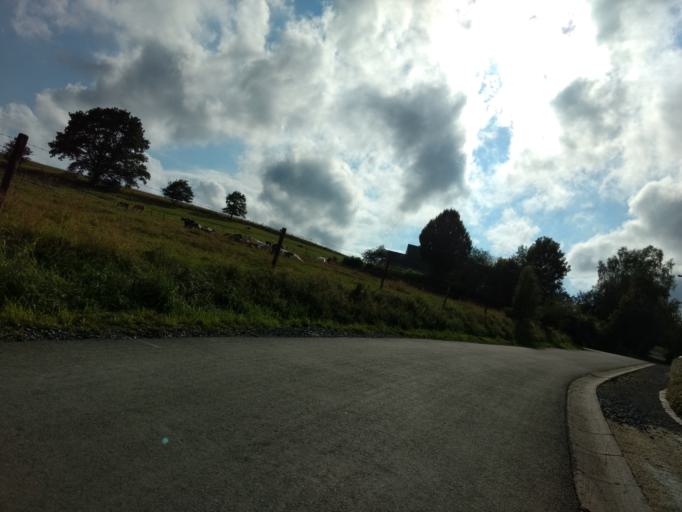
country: BE
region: Wallonia
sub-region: Province du Luxembourg
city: Houffalize
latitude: 50.1495
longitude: 5.7419
